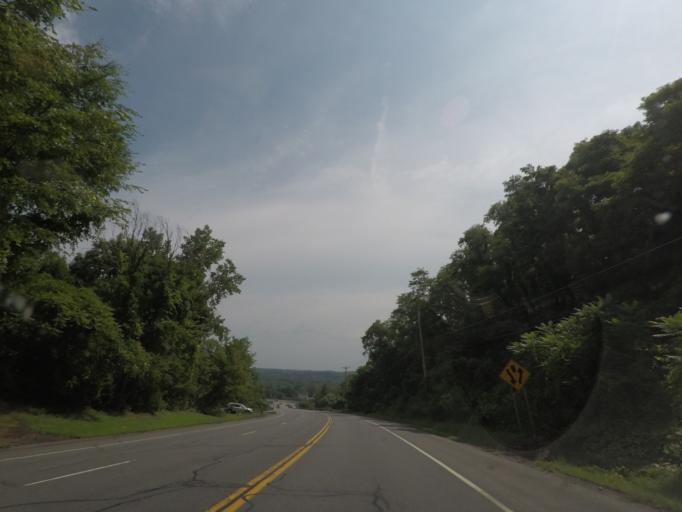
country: US
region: New York
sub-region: Saratoga County
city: Mechanicville
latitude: 42.8854
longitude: -73.6949
